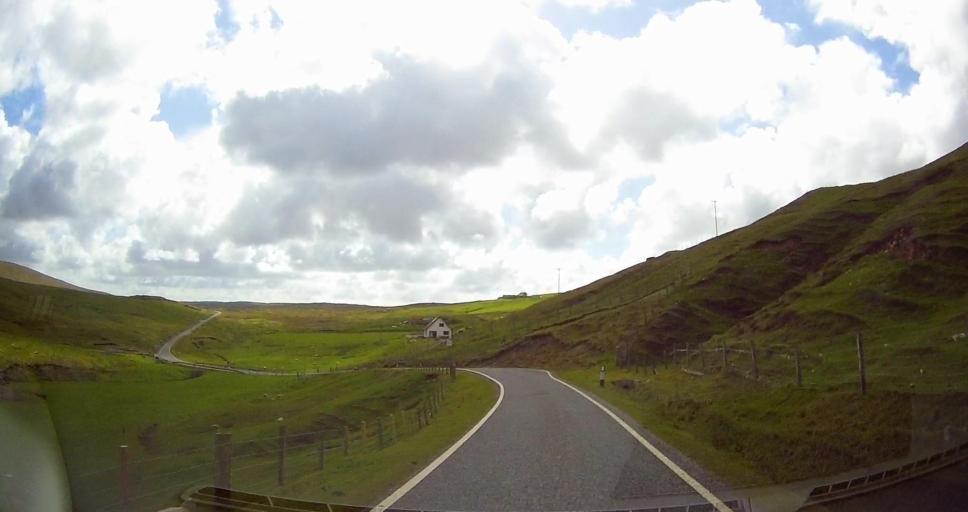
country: GB
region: Scotland
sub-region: Shetland Islands
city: Lerwick
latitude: 60.5267
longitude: -1.3703
